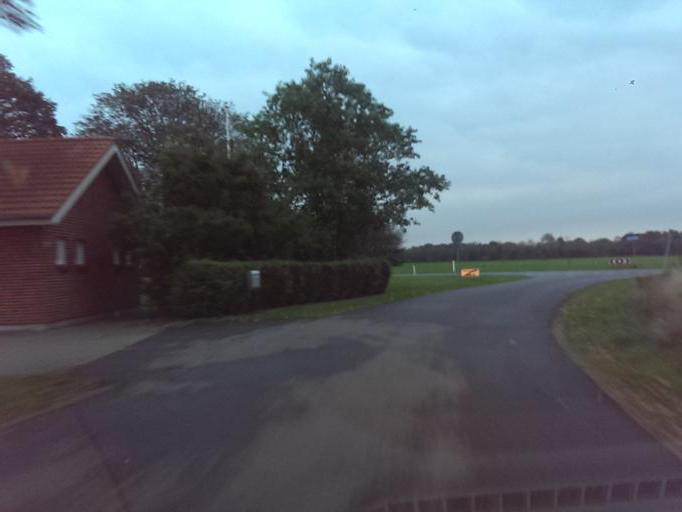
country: DK
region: South Denmark
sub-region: Esbjerg Kommune
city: Bramming
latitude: 55.4689
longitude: 8.7282
